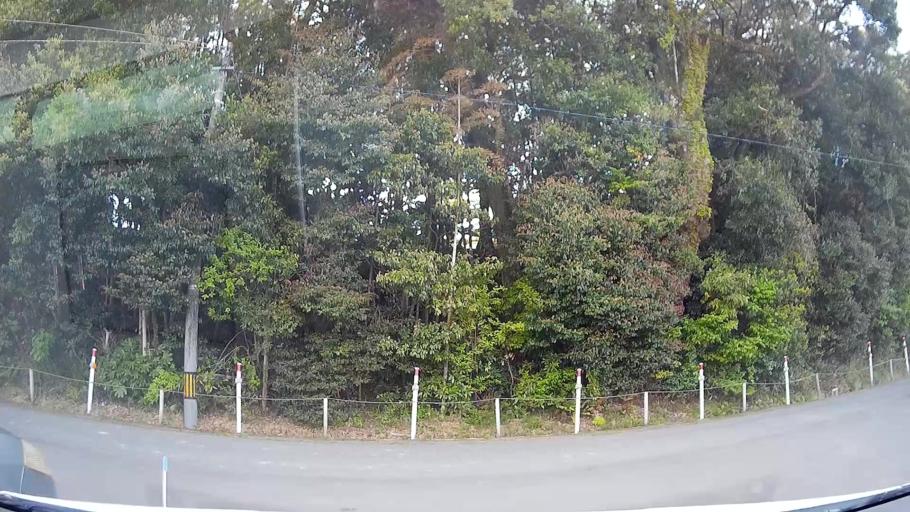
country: JP
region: Ishikawa
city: Hakui
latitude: 36.9545
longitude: 136.7773
